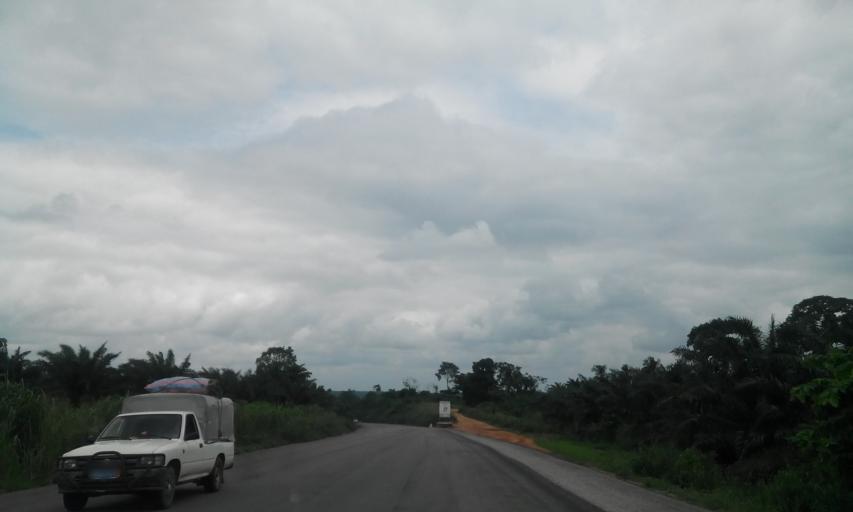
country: CI
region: Sud-Comoe
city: Mafere
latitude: 5.3176
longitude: -3.0523
